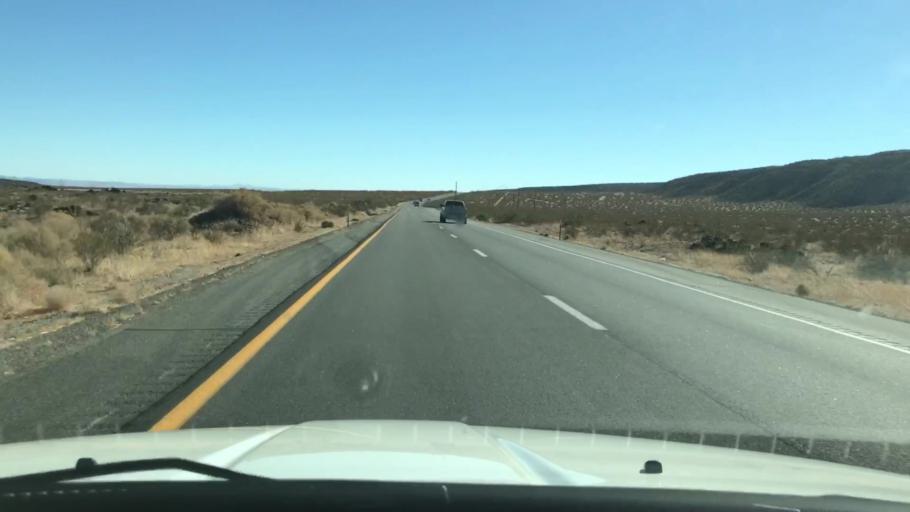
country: US
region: California
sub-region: Kern County
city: Inyokern
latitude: 35.8866
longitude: -117.8938
